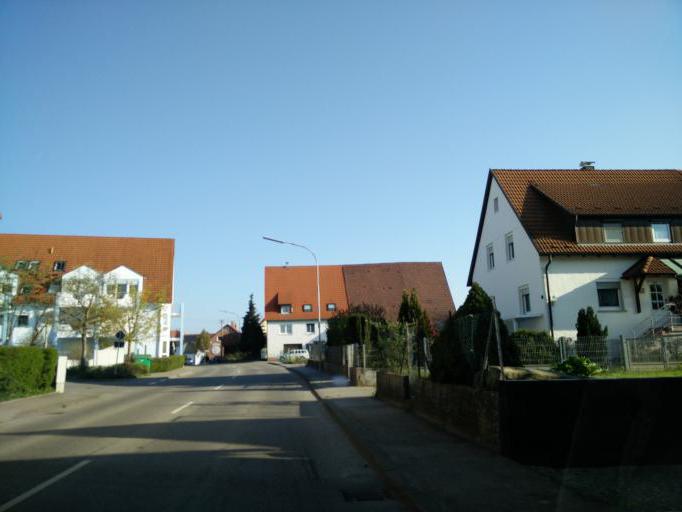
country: DE
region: Baden-Wuerttemberg
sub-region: Regierungsbezirk Stuttgart
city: Deckenpfronn
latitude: 48.6221
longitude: 8.8356
